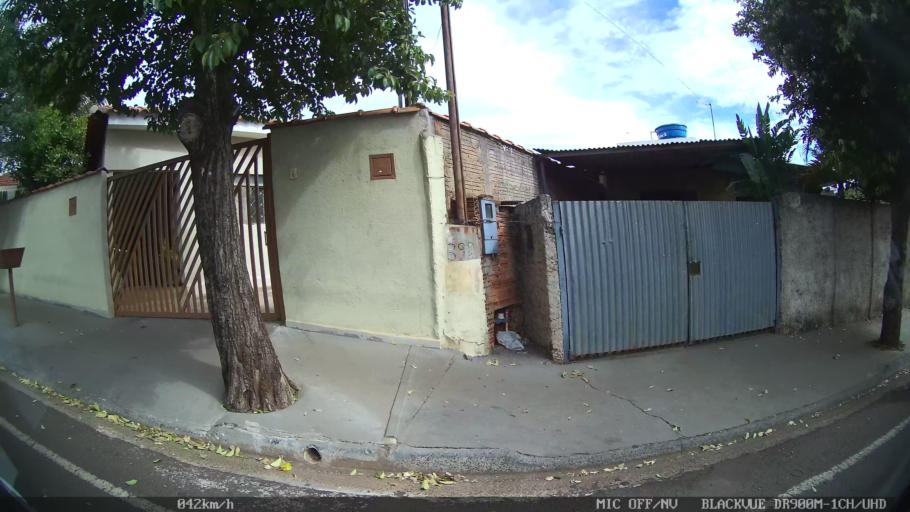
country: BR
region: Sao Paulo
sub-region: Catanduva
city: Catanduva
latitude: -21.1528
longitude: -48.9636
